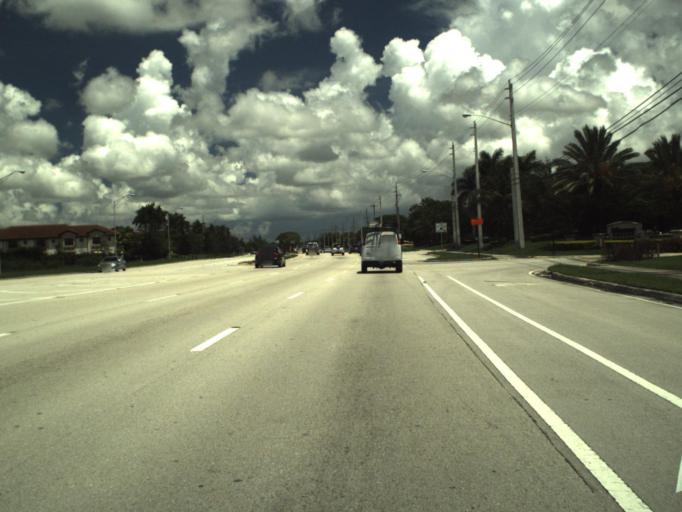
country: US
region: Florida
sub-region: Miami-Dade County
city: Country Club
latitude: 25.9787
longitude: -80.3094
